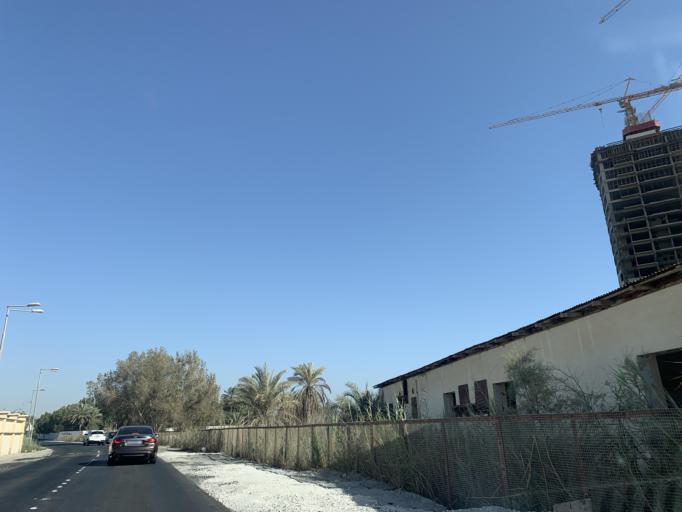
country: BH
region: Manama
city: Jidd Hafs
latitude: 26.2047
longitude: 50.4528
